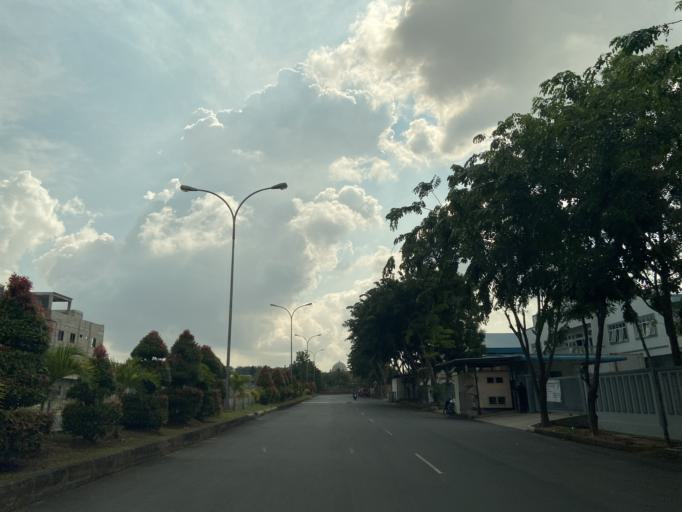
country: SG
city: Singapore
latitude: 1.1110
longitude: 104.0735
